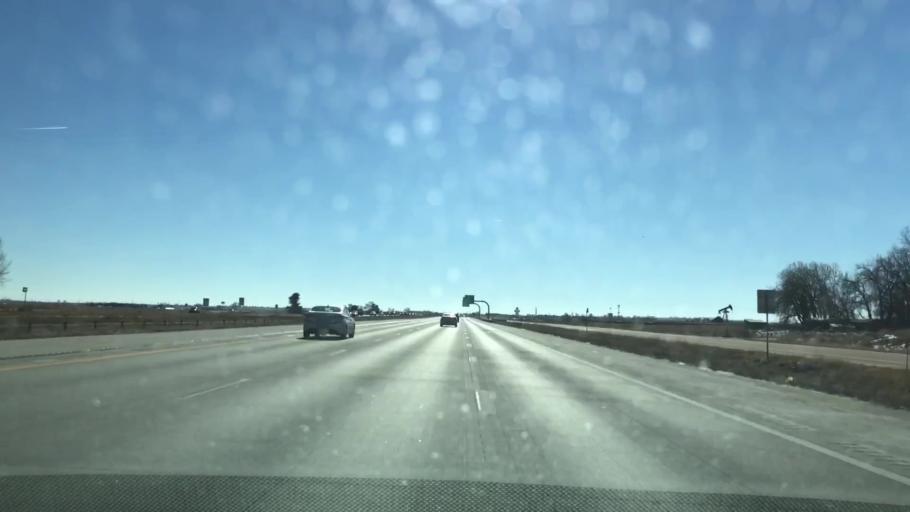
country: US
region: Colorado
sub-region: Weld County
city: Frederick
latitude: 40.1029
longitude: -104.9809
